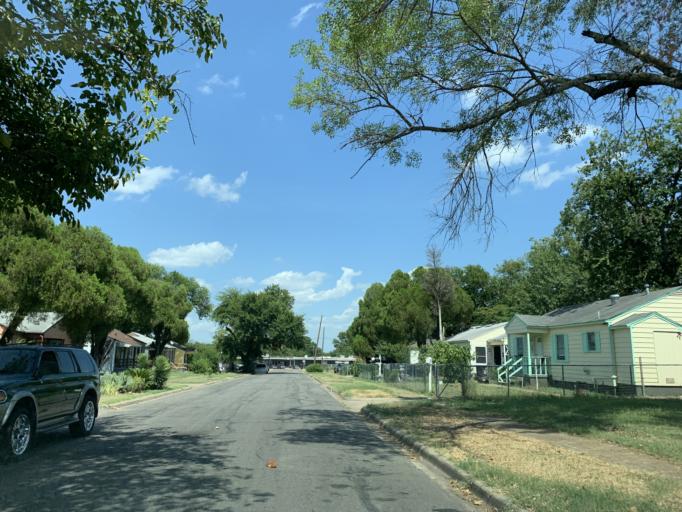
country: US
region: Texas
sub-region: Dallas County
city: Dallas
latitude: 32.7117
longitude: -96.7863
